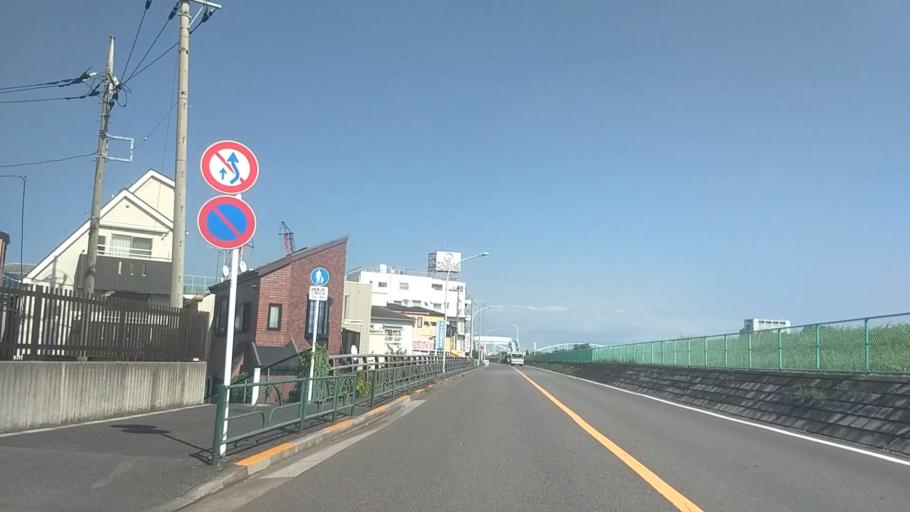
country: JP
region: Kanagawa
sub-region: Kawasaki-shi
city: Kawasaki
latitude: 35.5594
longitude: 139.6887
